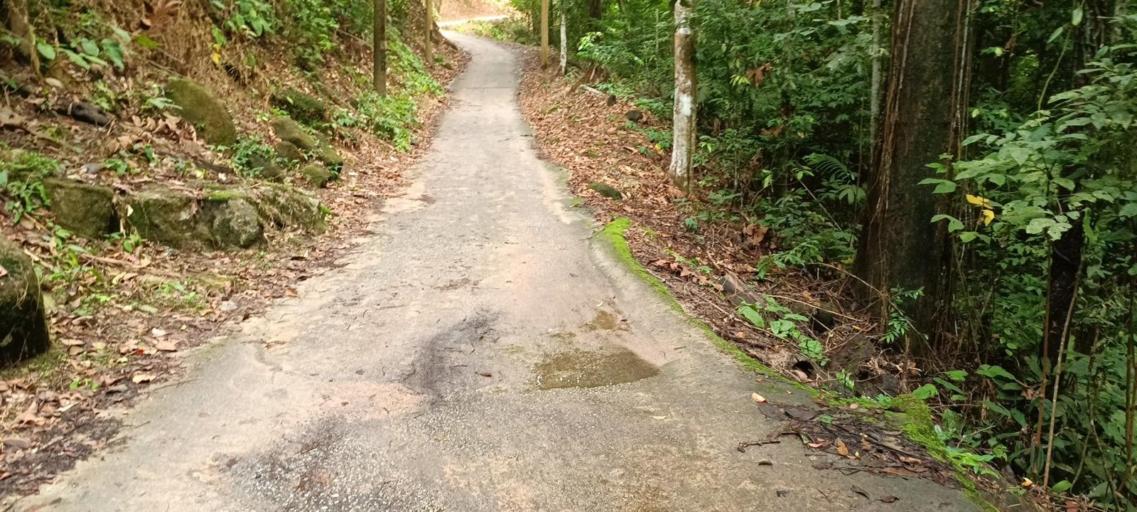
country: MY
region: Penang
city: Kampung Sungai Ara
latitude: 5.3891
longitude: 100.2577
